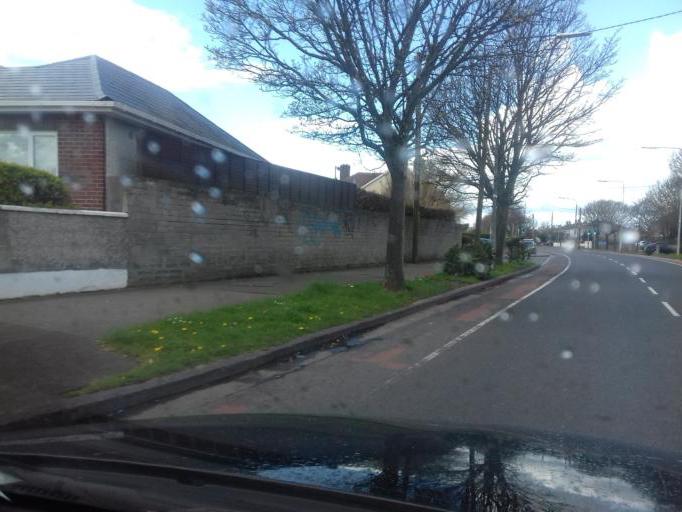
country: IE
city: Bayside
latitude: 53.3863
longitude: -6.1463
